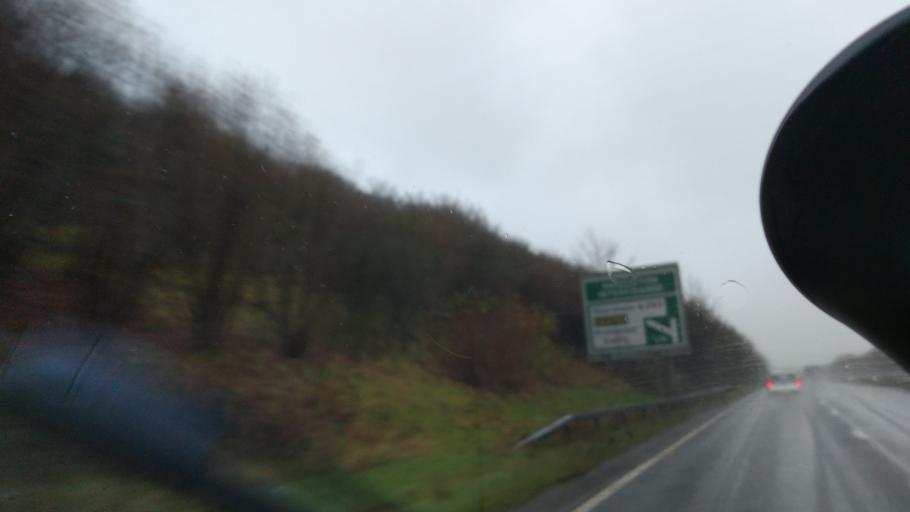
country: GB
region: England
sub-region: East Sussex
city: Portslade
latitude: 50.8554
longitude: -0.1927
